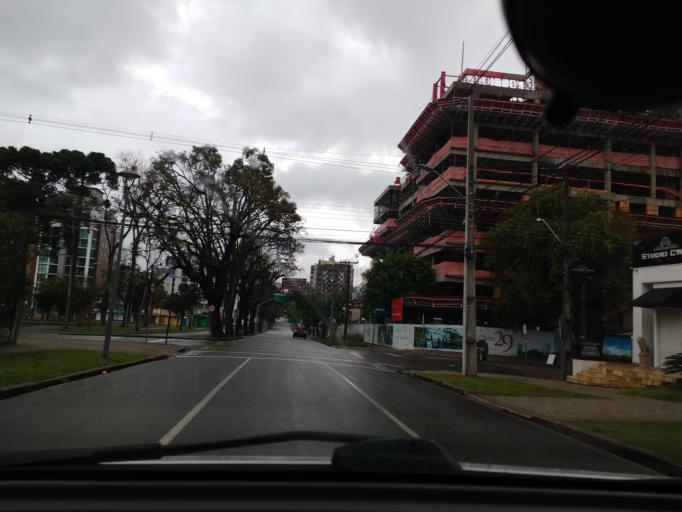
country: BR
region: Parana
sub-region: Curitiba
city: Curitiba
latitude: -25.4277
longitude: -49.2867
